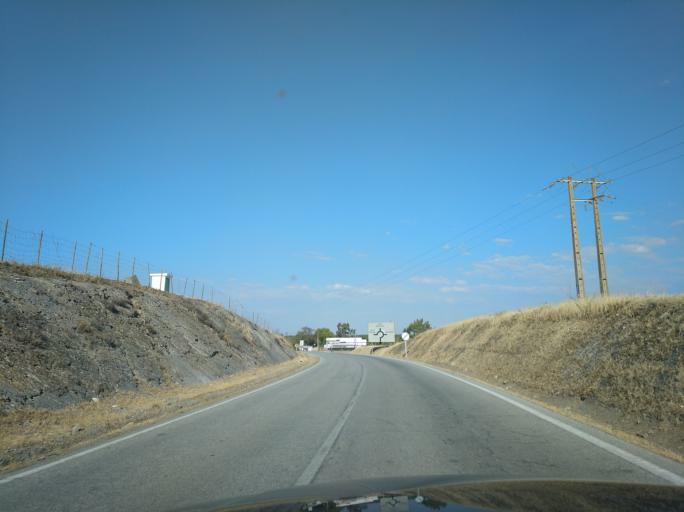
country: ES
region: Extremadura
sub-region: Provincia de Badajoz
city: Valencia del Mombuey
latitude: 38.2123
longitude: -7.2290
